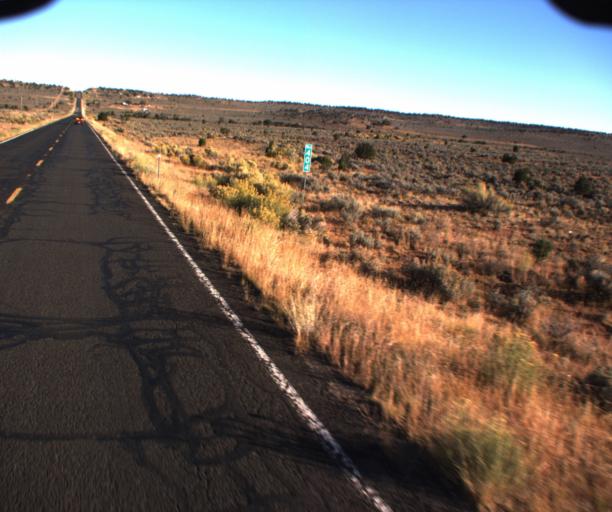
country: US
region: Arizona
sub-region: Apache County
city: Ganado
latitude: 35.5994
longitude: -109.5393
